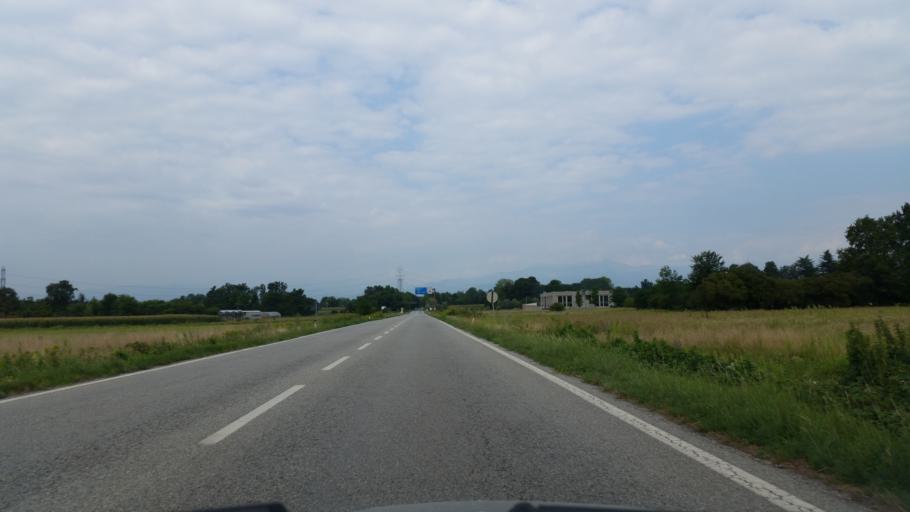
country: IT
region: Piedmont
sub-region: Provincia di Torino
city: Barone Canavese
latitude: 45.3080
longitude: 7.8703
